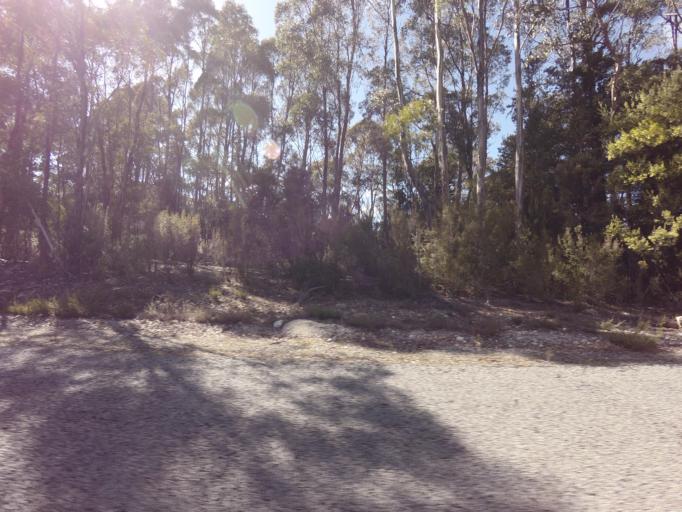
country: AU
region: Tasmania
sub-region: Huon Valley
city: Geeveston
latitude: -42.7682
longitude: 146.3974
